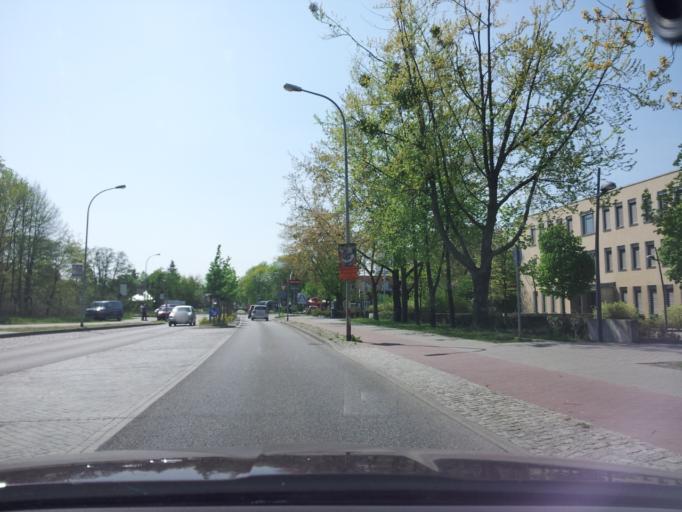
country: DE
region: Brandenburg
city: Kleinmachnow
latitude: 52.3956
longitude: 13.2401
